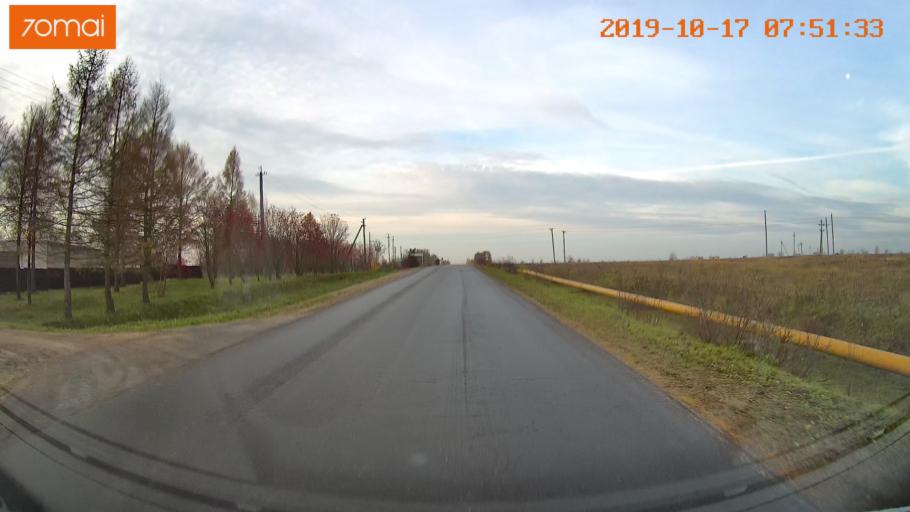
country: RU
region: Vladimir
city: Yur'yev-Pol'skiy
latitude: 56.4807
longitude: 39.6544
